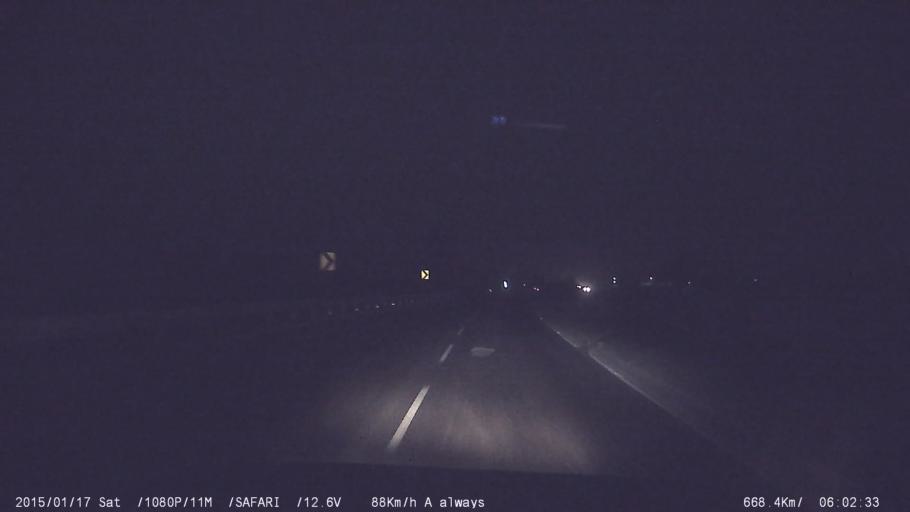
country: IN
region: Tamil Nadu
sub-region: Kancheepuram
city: Kanchipuram
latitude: 12.8899
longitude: 79.5944
